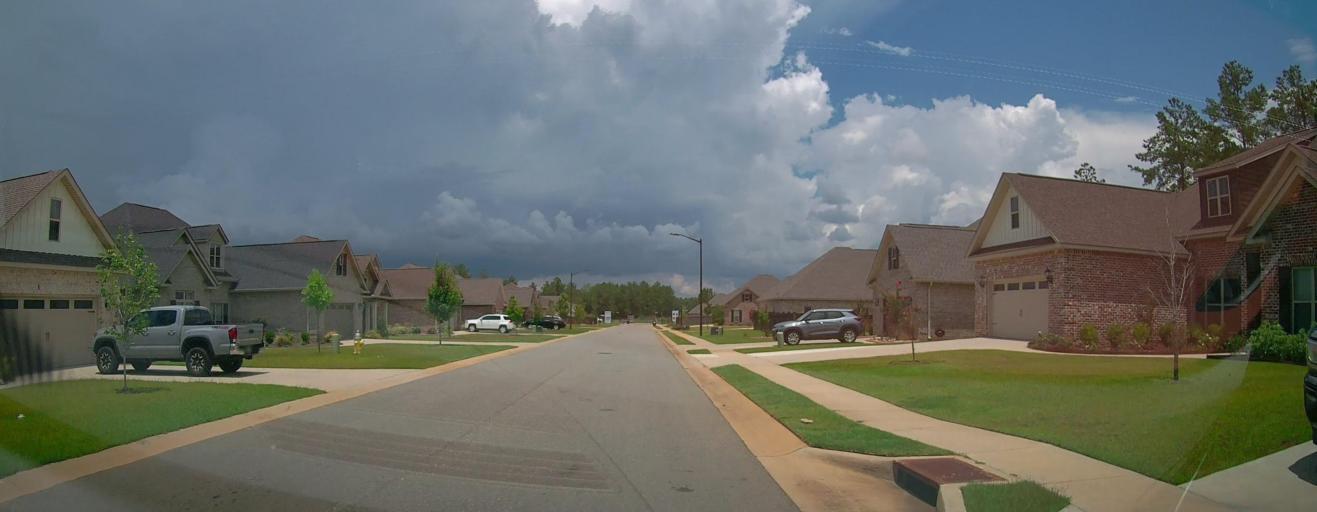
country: US
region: Georgia
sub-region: Houston County
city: Robins Air Force Base
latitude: 32.5129
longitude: -83.6309
